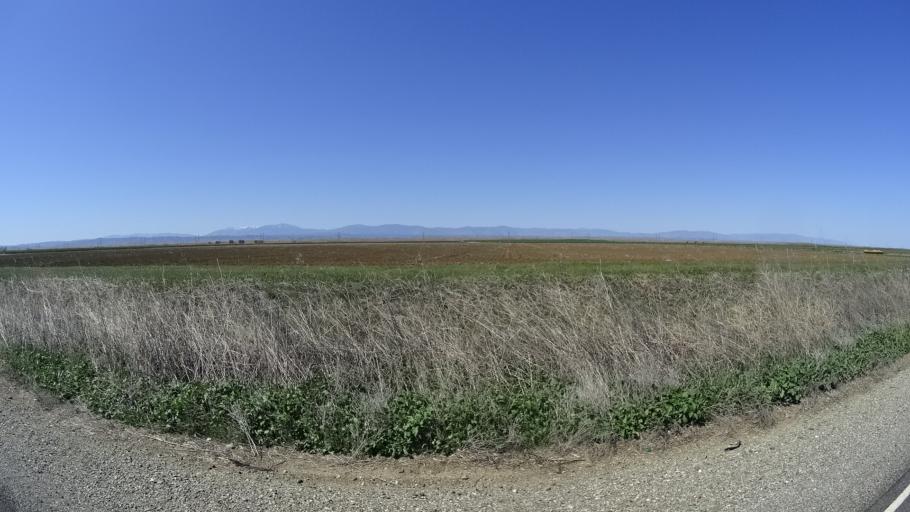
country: US
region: California
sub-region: Glenn County
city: Willows
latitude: 39.5592
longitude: -122.2495
